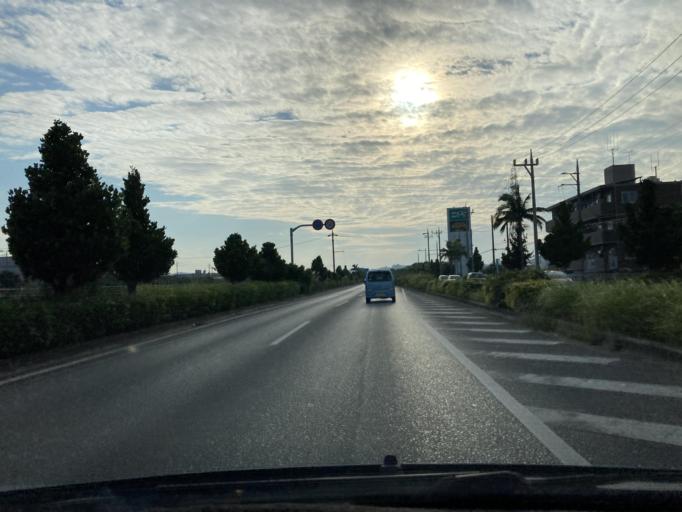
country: JP
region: Okinawa
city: Katsuren-haebaru
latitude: 26.3358
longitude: 127.8439
